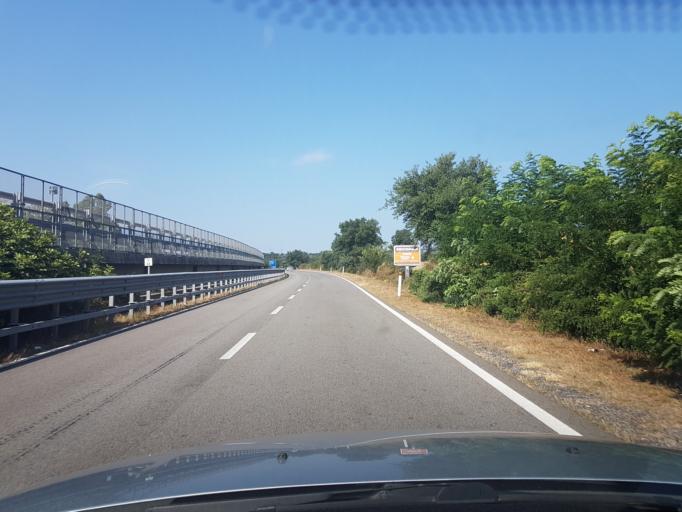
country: IT
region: Sardinia
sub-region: Provincia di Nuoro
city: Oniferi
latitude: 40.3110
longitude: 9.2043
